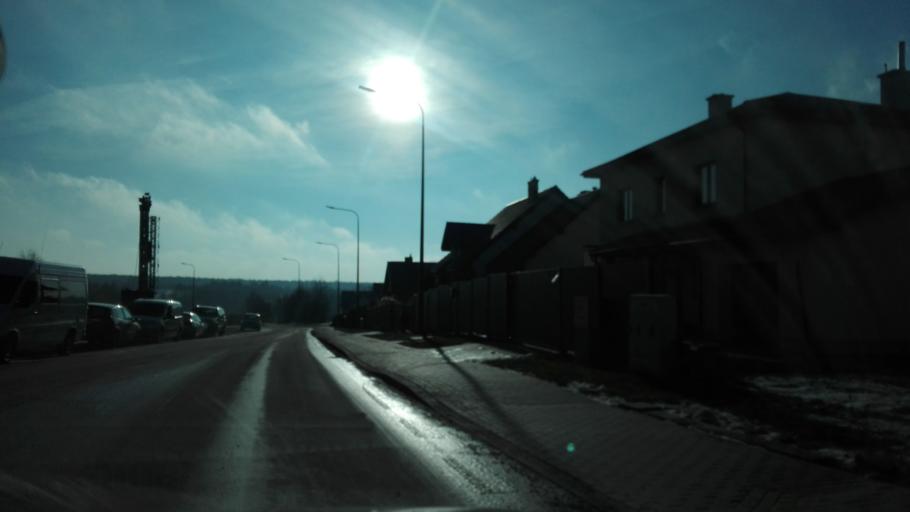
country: PL
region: Lublin Voivodeship
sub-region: Powiat lubelski
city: Kozubszczyzna
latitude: 51.2230
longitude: 22.4928
